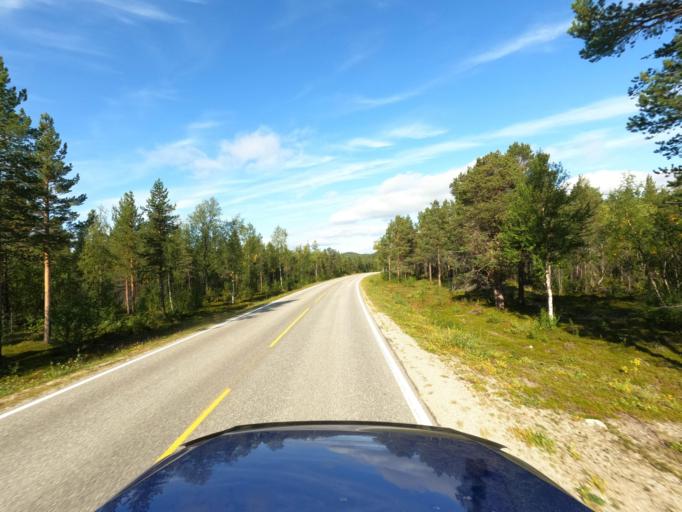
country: NO
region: Finnmark Fylke
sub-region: Porsanger
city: Lakselv
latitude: 69.8171
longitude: 25.1574
